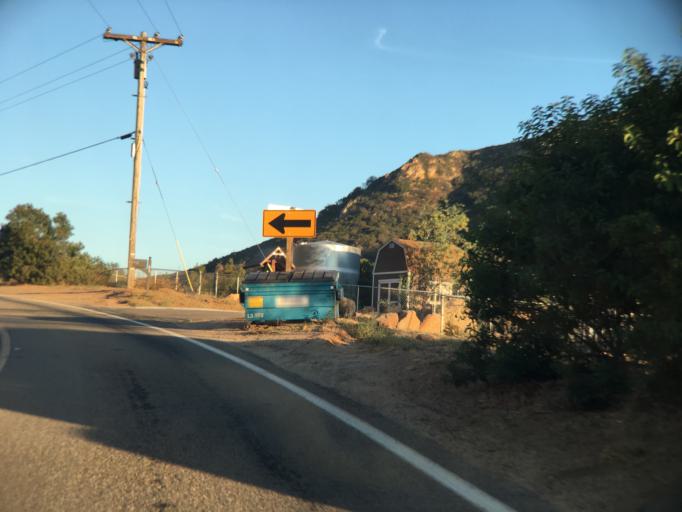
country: US
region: California
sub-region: San Diego County
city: Harbison Canyon
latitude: 32.8066
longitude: -116.7984
